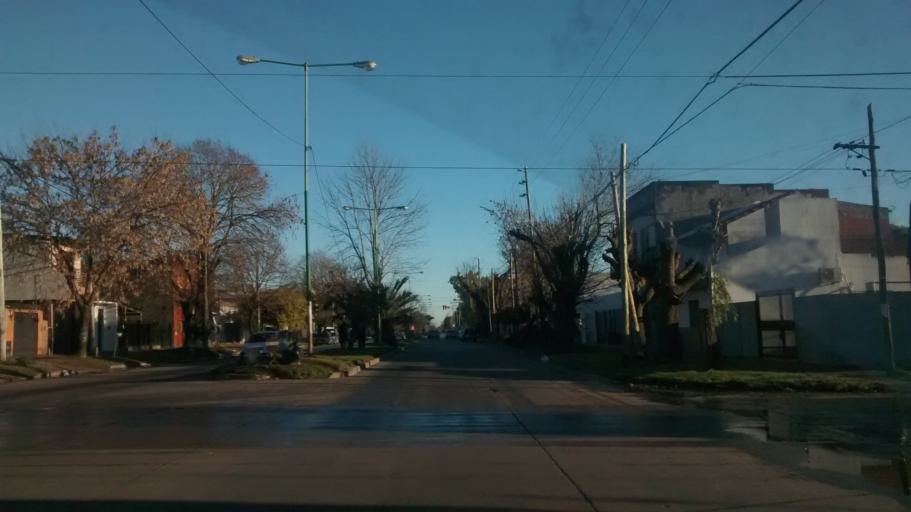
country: AR
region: Buenos Aires
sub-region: Partido de La Plata
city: La Plata
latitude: -34.9561
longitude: -57.9774
